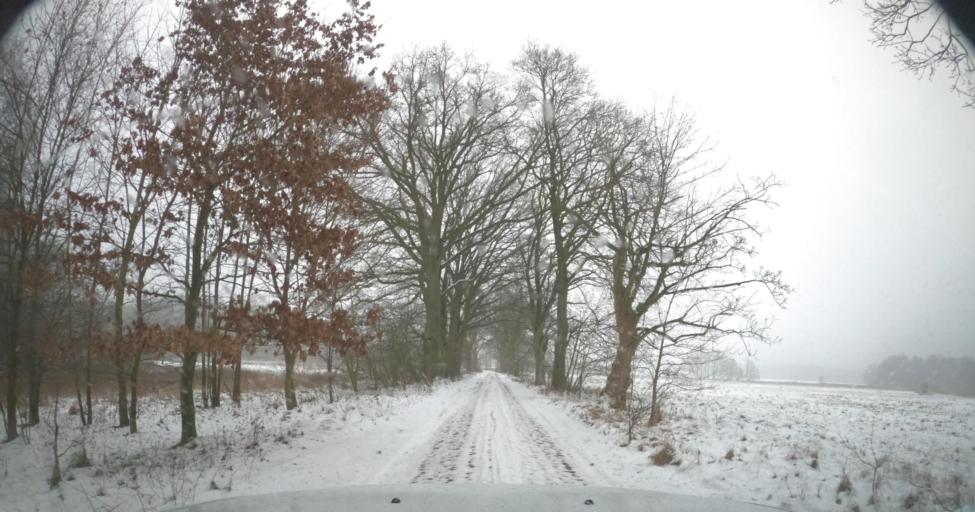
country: PL
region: West Pomeranian Voivodeship
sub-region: Powiat kamienski
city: Golczewo
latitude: 53.7700
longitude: 14.9445
